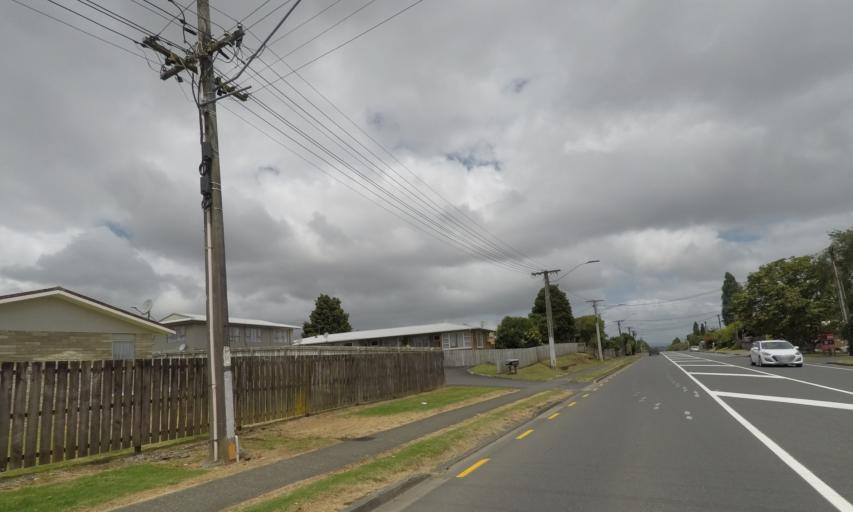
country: NZ
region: Northland
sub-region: Whangarei
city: Whangarei
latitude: -35.6938
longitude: 174.3111
